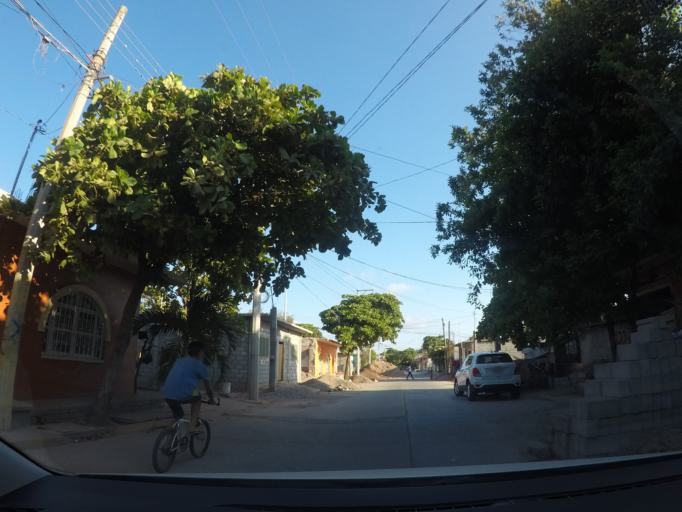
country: MX
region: Oaxaca
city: Juchitan de Zaragoza
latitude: 16.4370
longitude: -95.0289
